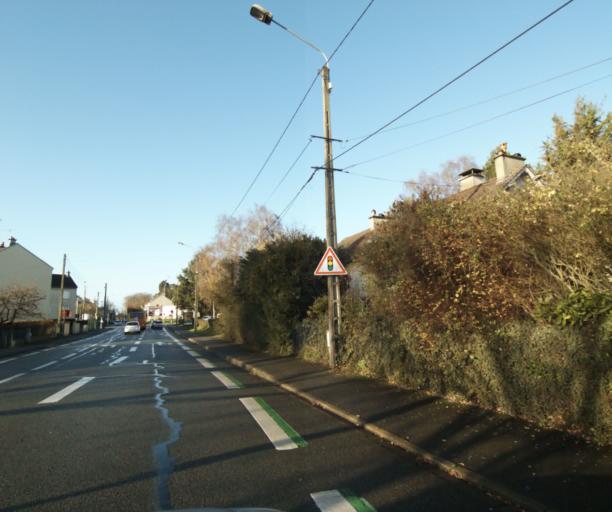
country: FR
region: Pays de la Loire
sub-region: Departement de la Sarthe
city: Coulaines
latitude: 48.0147
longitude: 0.2228
